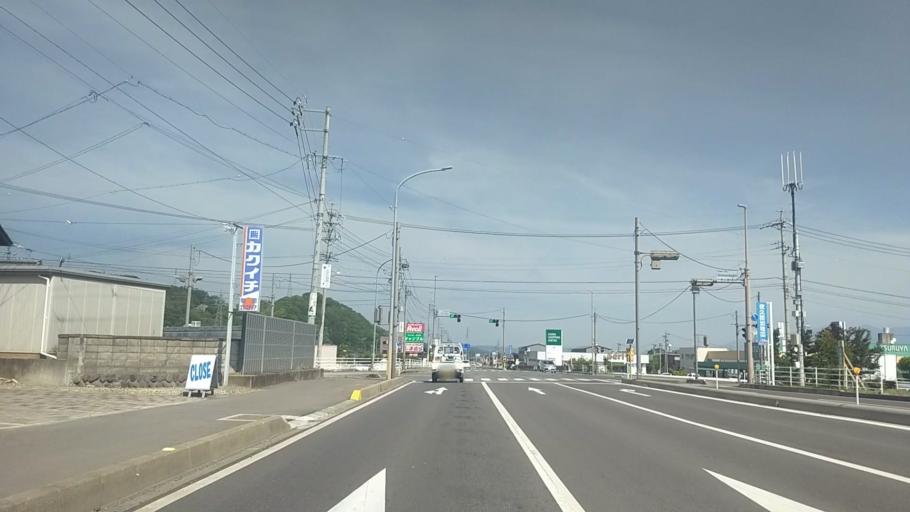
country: JP
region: Nagano
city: Saku
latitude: 36.1937
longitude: 138.4783
